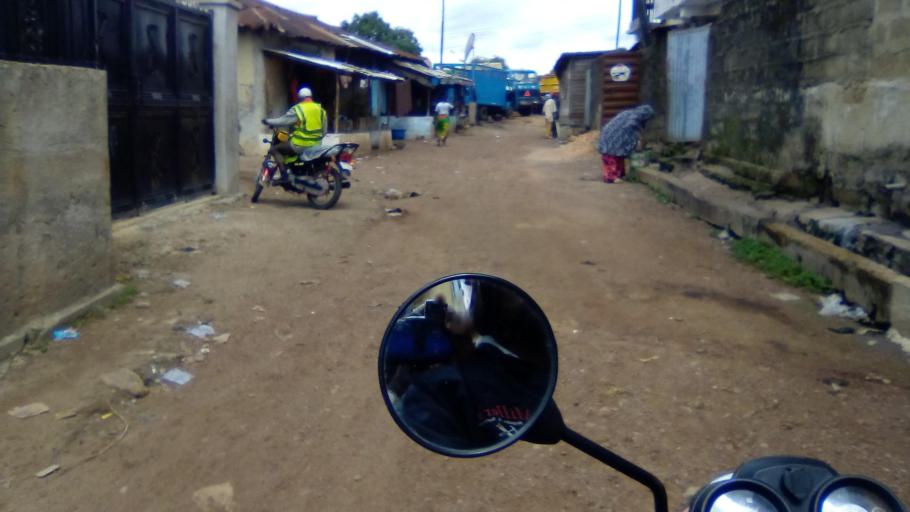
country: SL
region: Southern Province
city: Bo
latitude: 7.9626
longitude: -11.7341
